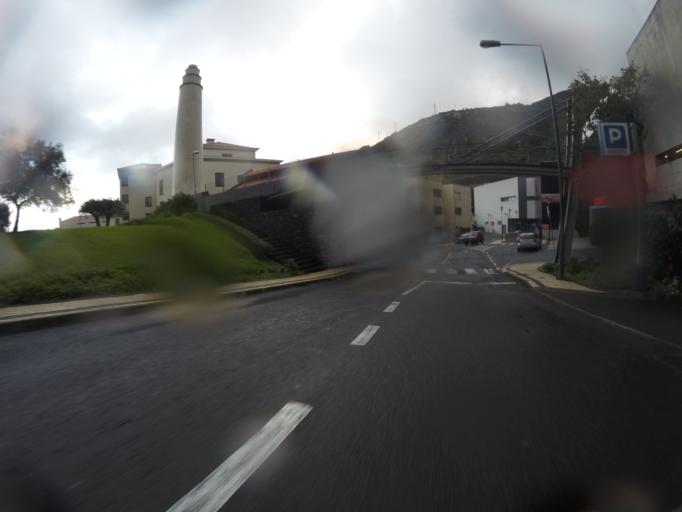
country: PT
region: Madeira
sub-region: Machico
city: Machico
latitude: 32.7209
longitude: -16.7683
